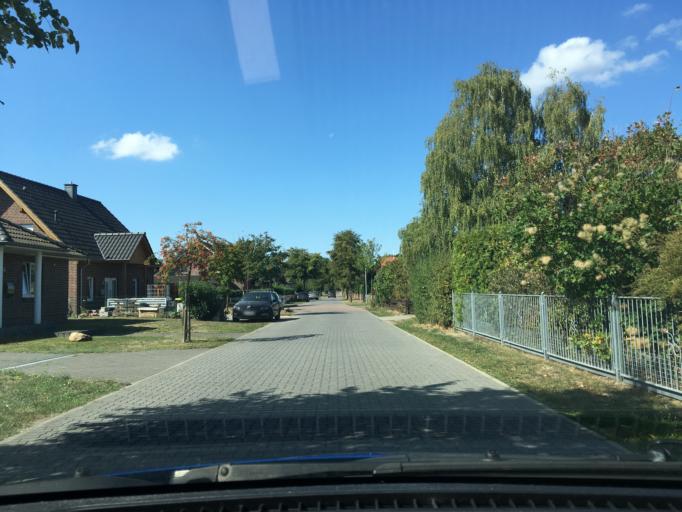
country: DE
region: Lower Saxony
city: Winsen (Aller)
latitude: 52.6704
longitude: 9.9092
